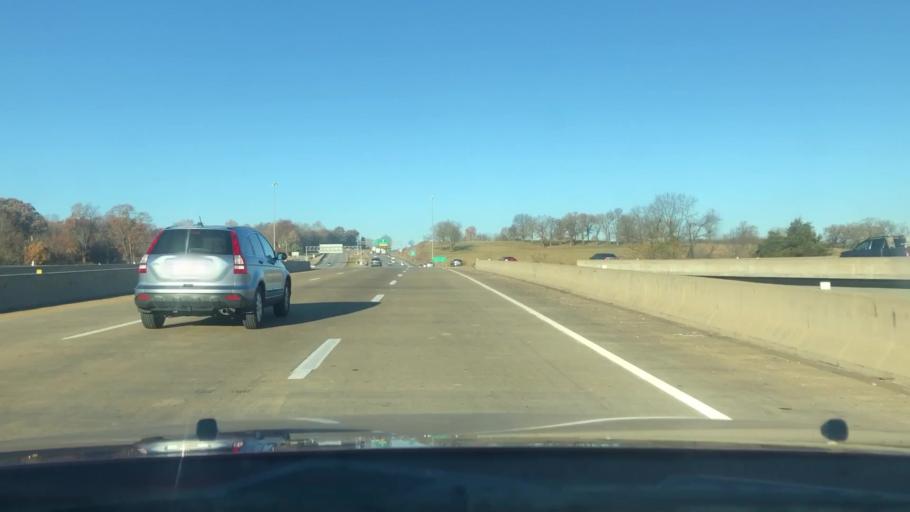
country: US
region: Missouri
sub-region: Christian County
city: Nixa
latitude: 37.1297
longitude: -93.2346
